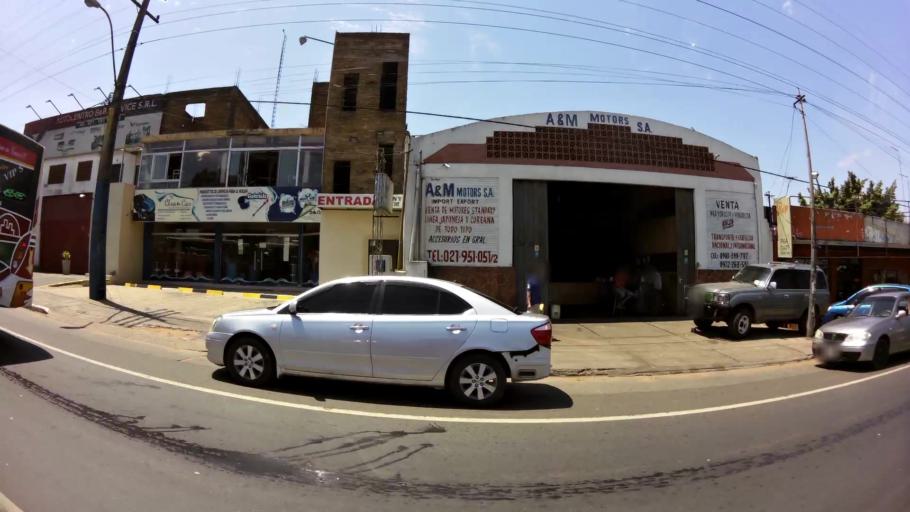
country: PY
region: Central
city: Nemby
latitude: -25.3791
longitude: -57.5540
